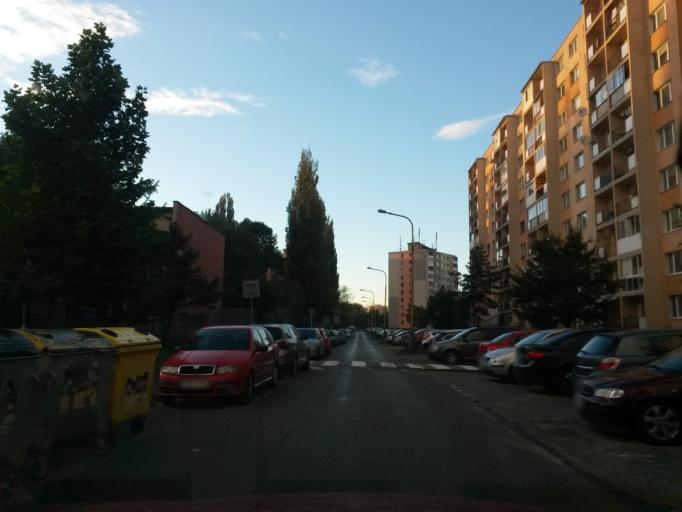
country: SK
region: Kosicky
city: Kosice
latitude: 48.6852
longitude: 21.2928
